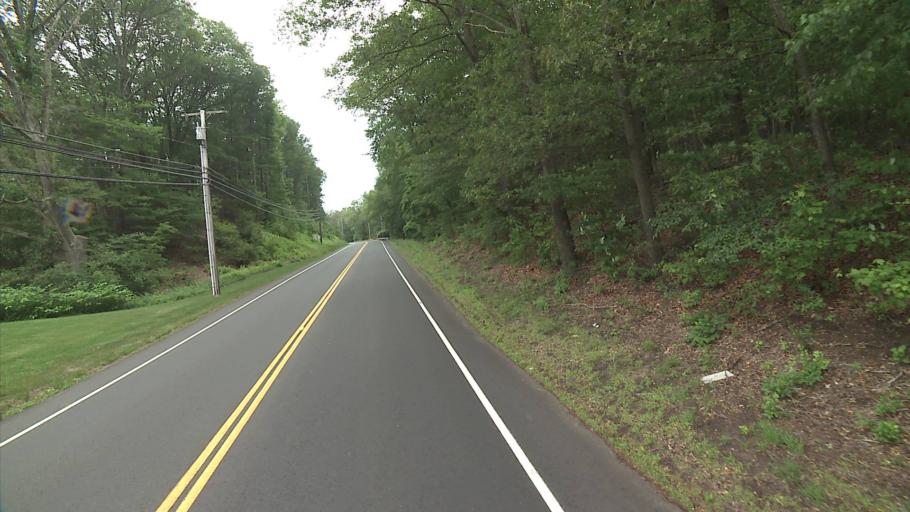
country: US
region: Connecticut
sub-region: Hartford County
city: Manchester
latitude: 41.7096
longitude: -72.4961
